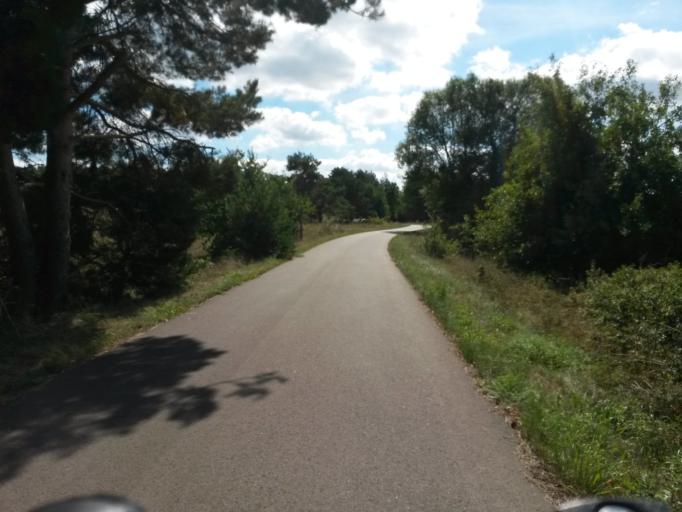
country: DE
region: Brandenburg
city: Templin
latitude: 53.1558
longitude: 13.5278
